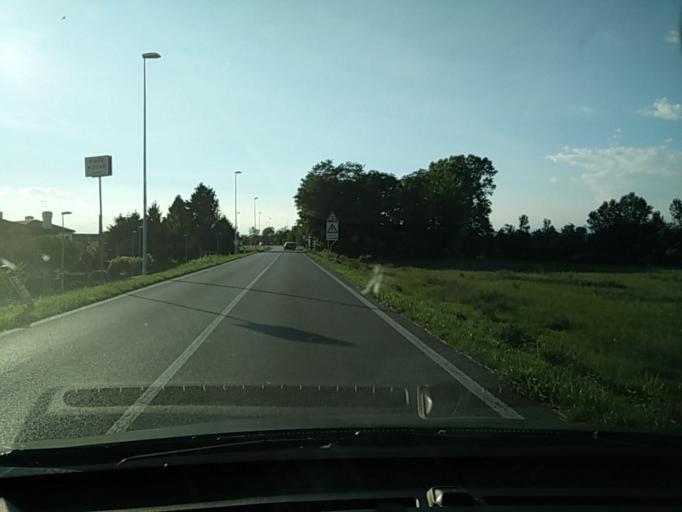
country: IT
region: Veneto
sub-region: Provincia di Venezia
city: Eraclea
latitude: 45.5842
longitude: 12.6442
